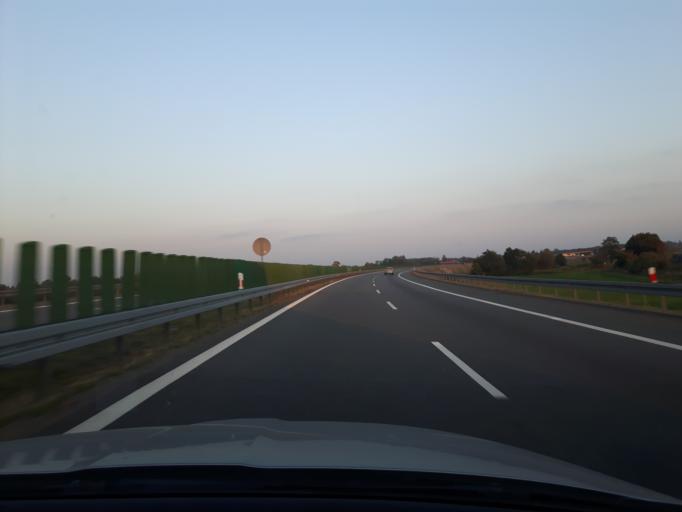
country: PL
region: Warmian-Masurian Voivodeship
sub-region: Powiat elblaski
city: Paslek
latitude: 54.0908
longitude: 19.5899
